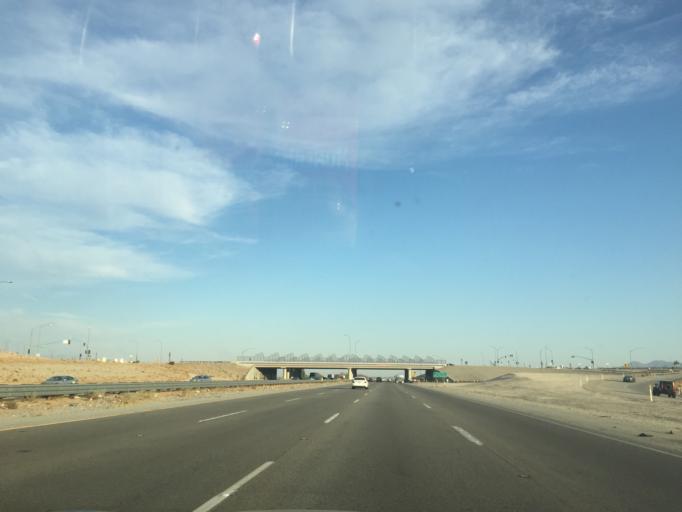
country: US
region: California
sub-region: Riverside County
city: Cathedral City
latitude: 33.8509
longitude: -116.4613
